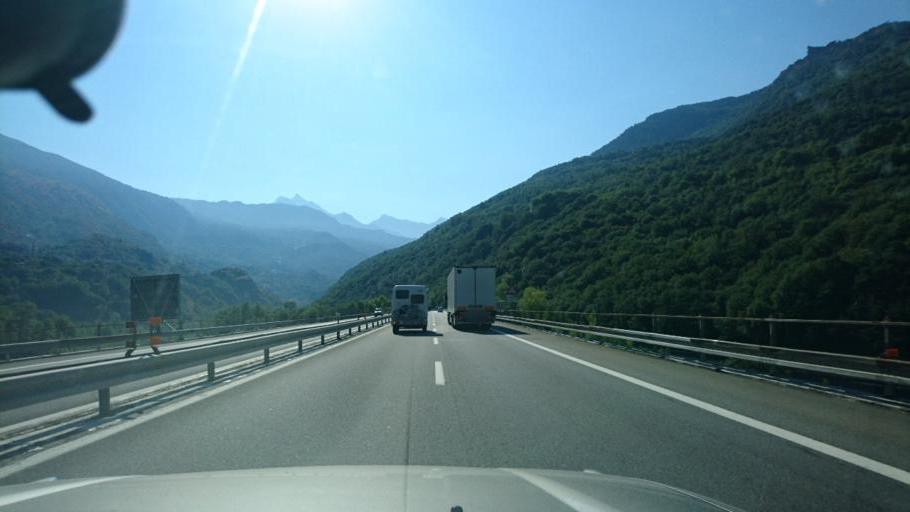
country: IT
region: Aosta Valley
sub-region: Valle d'Aosta
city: Saint-Vincent
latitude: 45.7437
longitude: 7.6365
